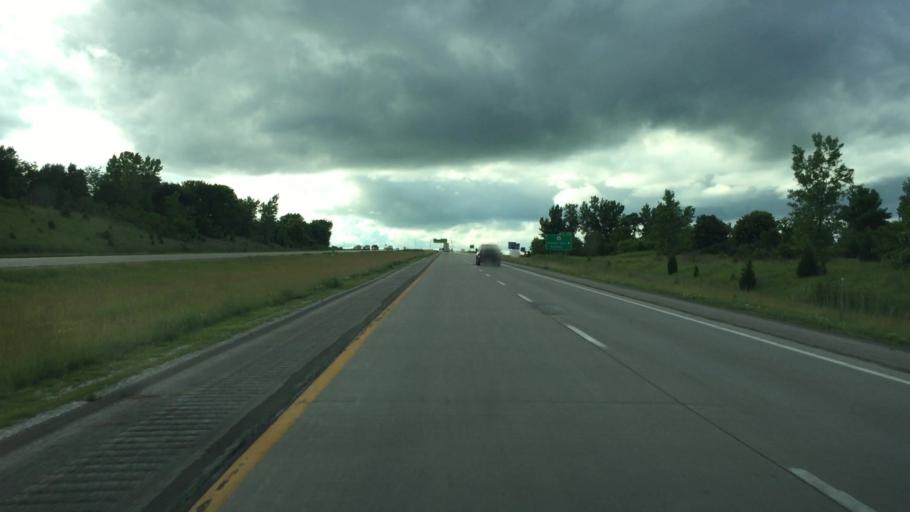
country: US
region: Iowa
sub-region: Polk County
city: Altoona
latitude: 41.6378
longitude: -93.5061
